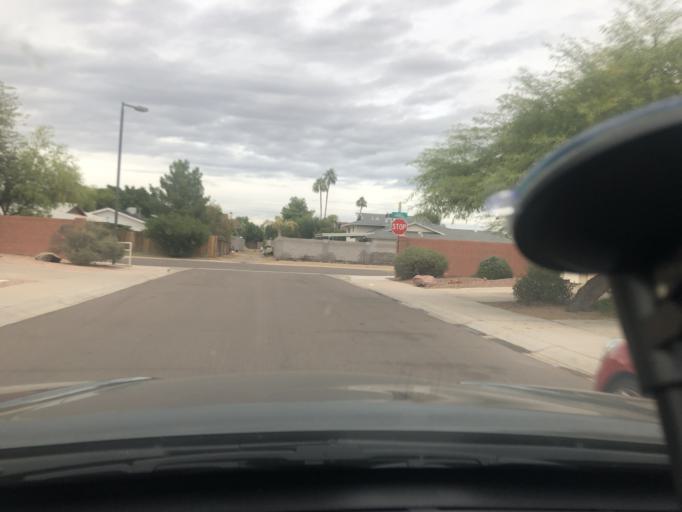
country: US
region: Arizona
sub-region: Maricopa County
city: Scottsdale
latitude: 33.4836
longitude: -111.8951
